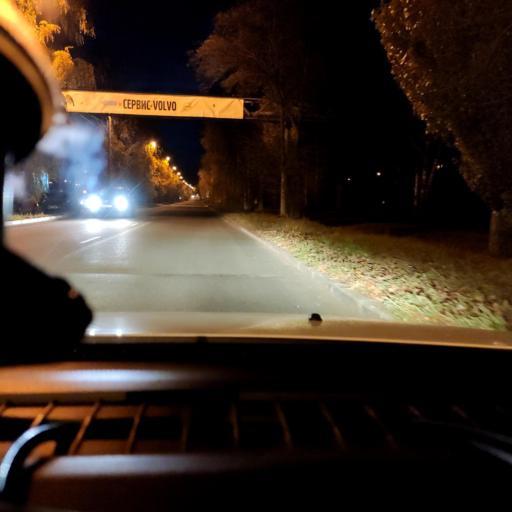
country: RU
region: Samara
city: Bereza
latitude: 53.5127
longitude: 50.1434
